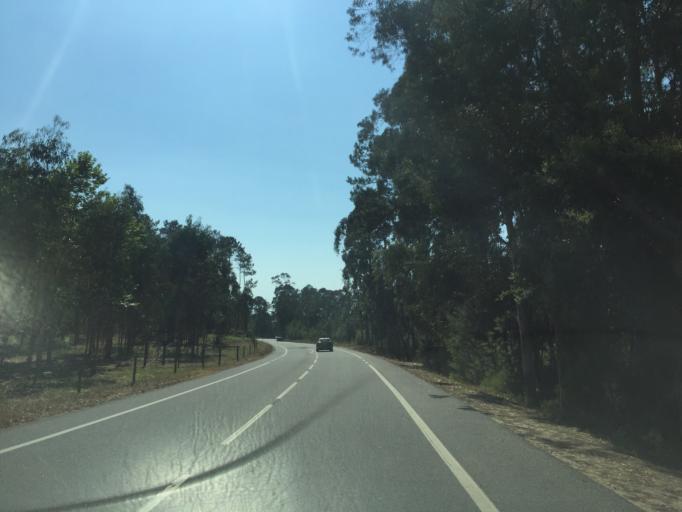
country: PT
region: Coimbra
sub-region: Cantanhede
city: Cantanhede
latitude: 40.3396
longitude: -8.6169
